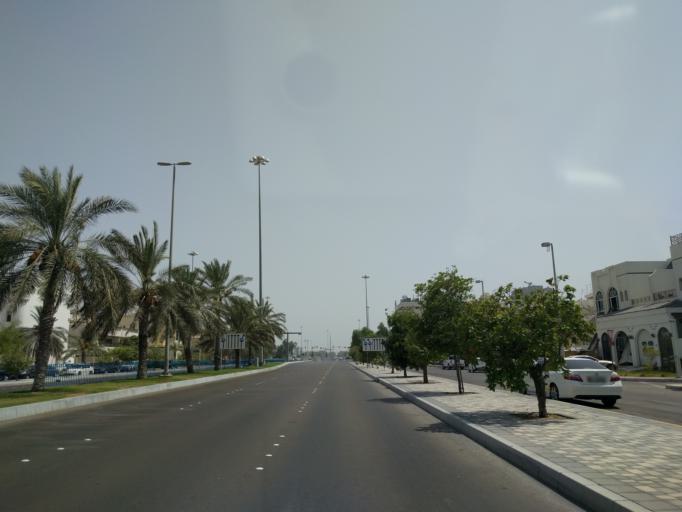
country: AE
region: Abu Dhabi
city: Abu Dhabi
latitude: 24.4405
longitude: 54.4174
